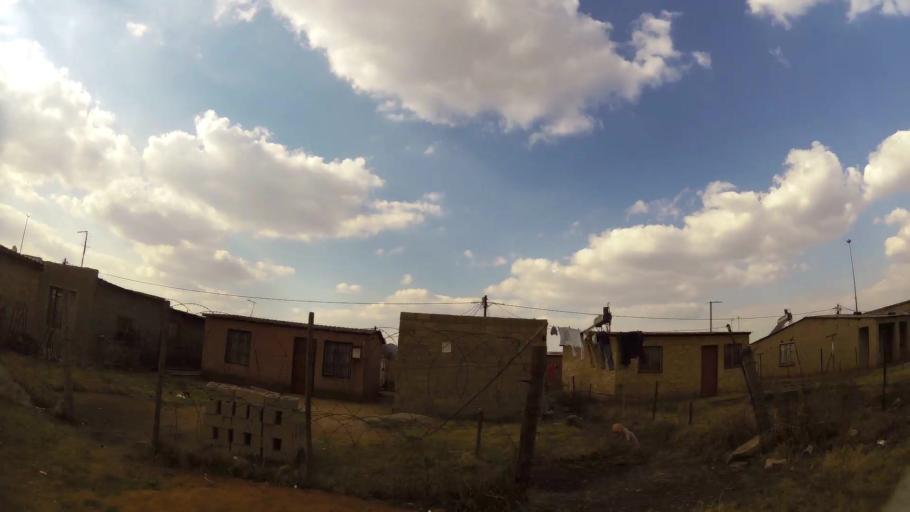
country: ZA
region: Mpumalanga
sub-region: Nkangala District Municipality
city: Delmas
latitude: -26.1388
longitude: 28.6956
